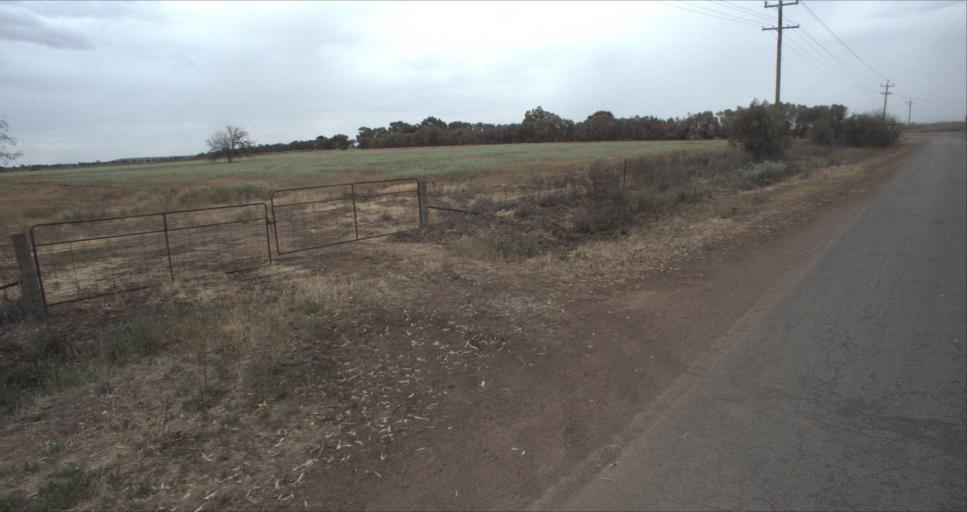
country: AU
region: New South Wales
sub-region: Leeton
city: Leeton
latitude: -34.4052
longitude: 146.3414
